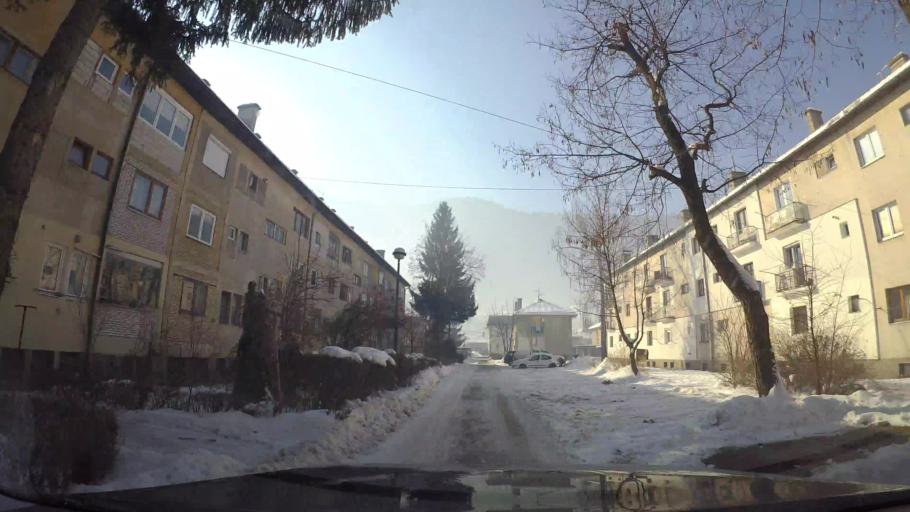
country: BA
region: Federation of Bosnia and Herzegovina
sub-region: Kanton Sarajevo
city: Sarajevo
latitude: 43.7993
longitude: 18.3088
